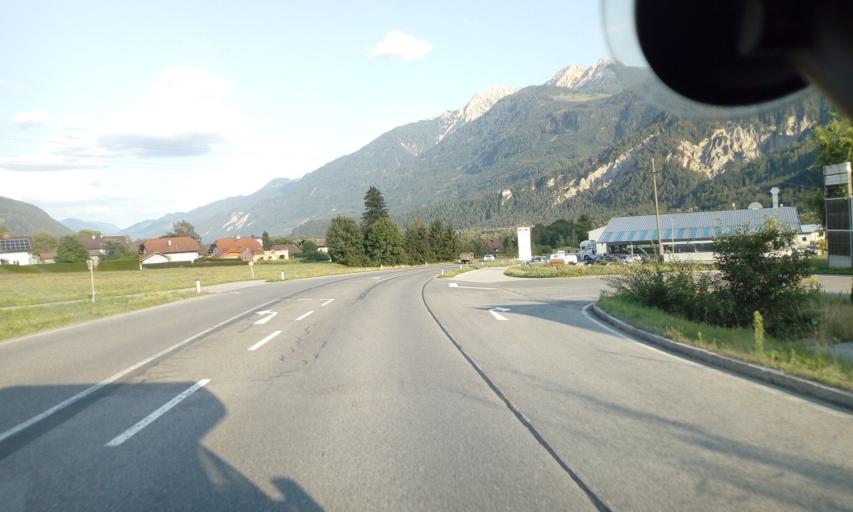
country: AT
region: Carinthia
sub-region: Politischer Bezirk Spittal an der Drau
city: Oberdrauburg
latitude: 46.7465
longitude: 12.9965
